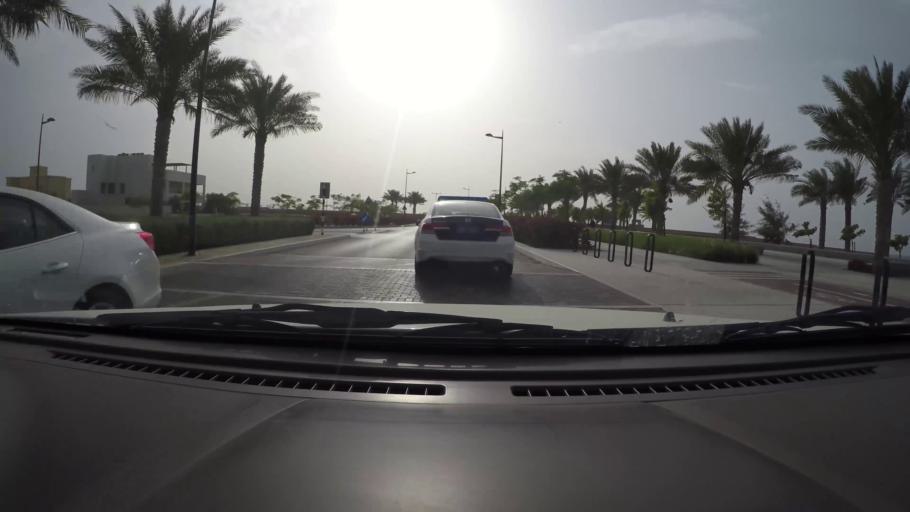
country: OM
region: Muhafazat Masqat
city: As Sib al Jadidah
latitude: 23.6945
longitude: 58.1567
